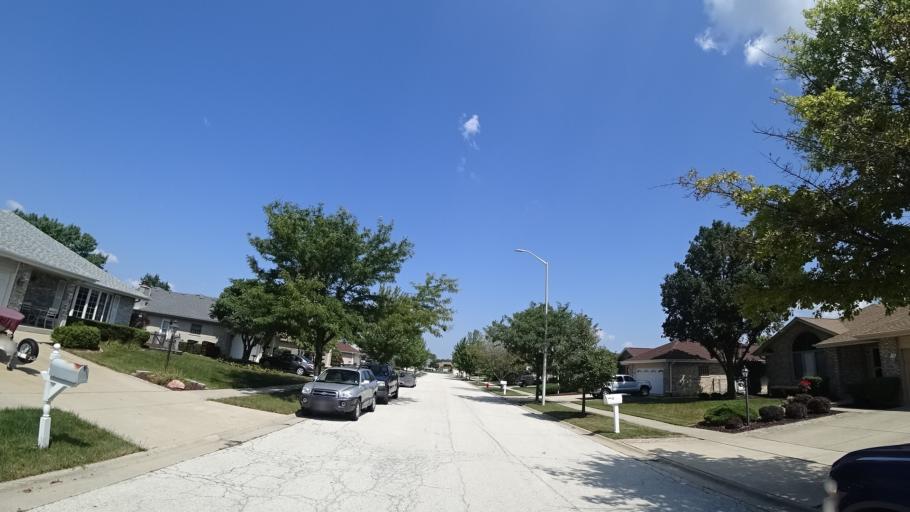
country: US
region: Illinois
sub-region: Cook County
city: Tinley Park
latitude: 41.6085
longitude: -87.7882
